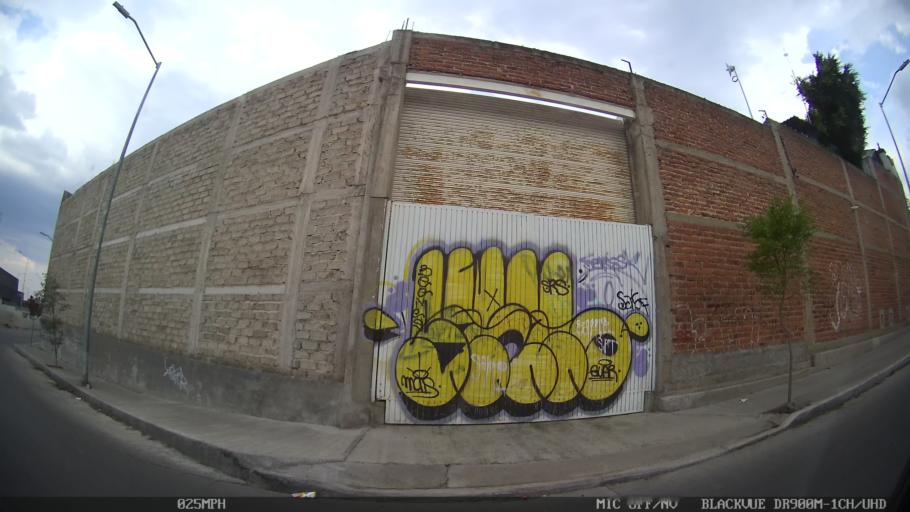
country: MX
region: Jalisco
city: Tlaquepaque
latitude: 20.6177
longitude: -103.2780
